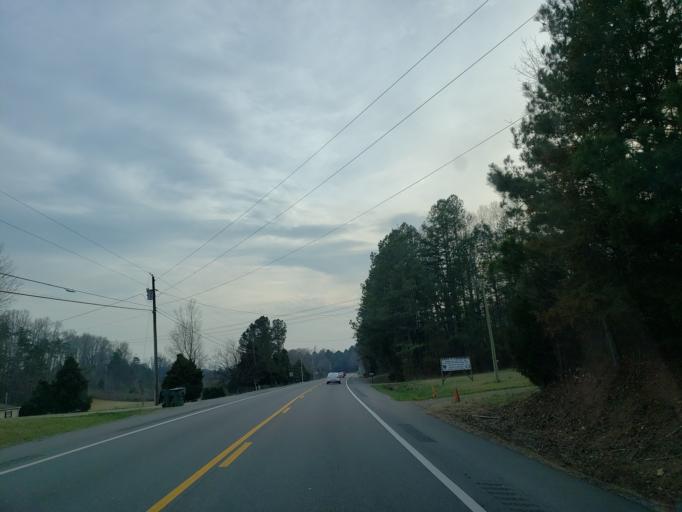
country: US
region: Tennessee
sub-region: Hamilton County
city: Apison
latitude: 34.9967
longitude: -84.9259
